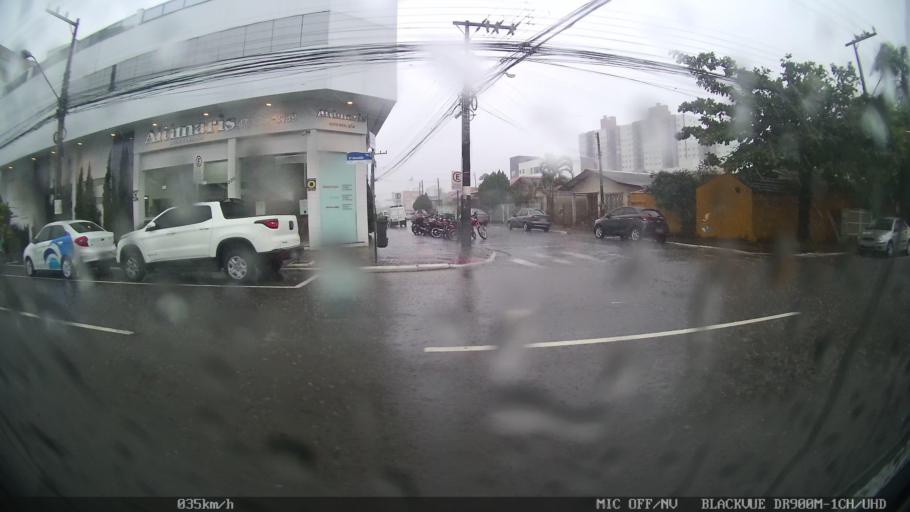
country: BR
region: Santa Catarina
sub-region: Balneario Camboriu
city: Balneario Camboriu
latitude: -26.9927
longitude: -48.6421
